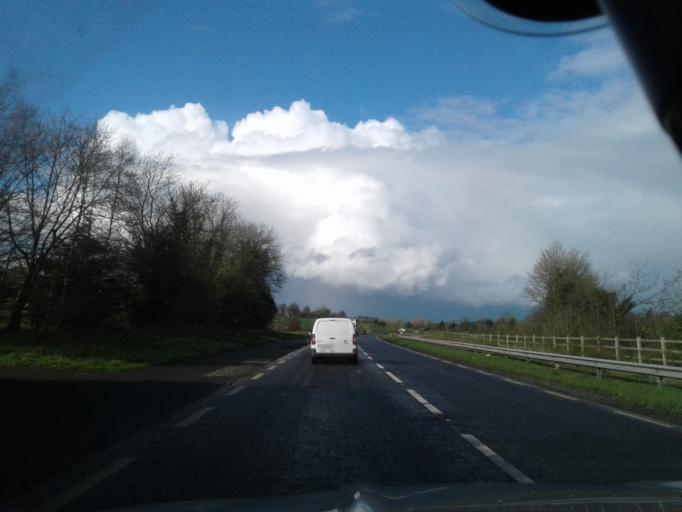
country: IE
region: Ulster
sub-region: County Monaghan
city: Monaghan
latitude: 54.3042
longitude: -6.9682
